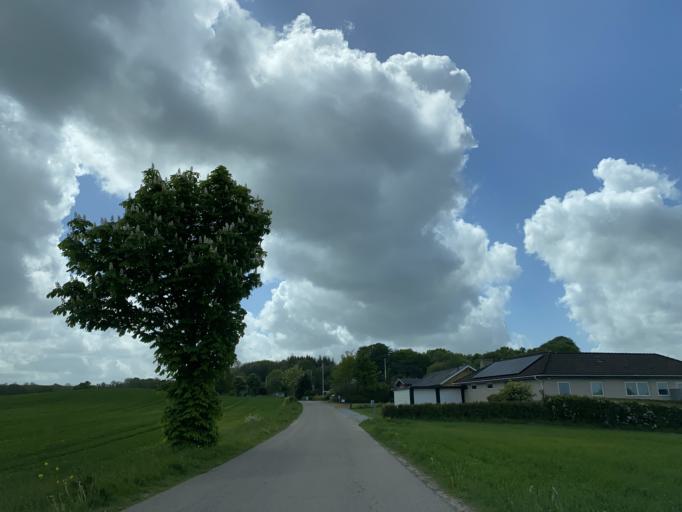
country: DK
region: South Denmark
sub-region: Aabenraa Kommune
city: Lojt Kirkeby
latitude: 55.0122
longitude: 9.4908
